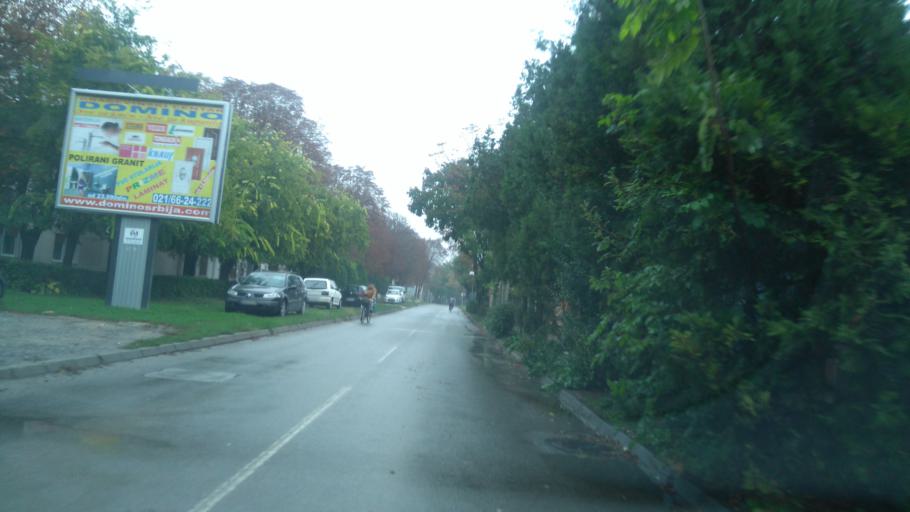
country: RS
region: Autonomna Pokrajina Vojvodina
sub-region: Juznobacki Okrug
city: Becej
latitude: 45.6131
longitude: 20.0506
